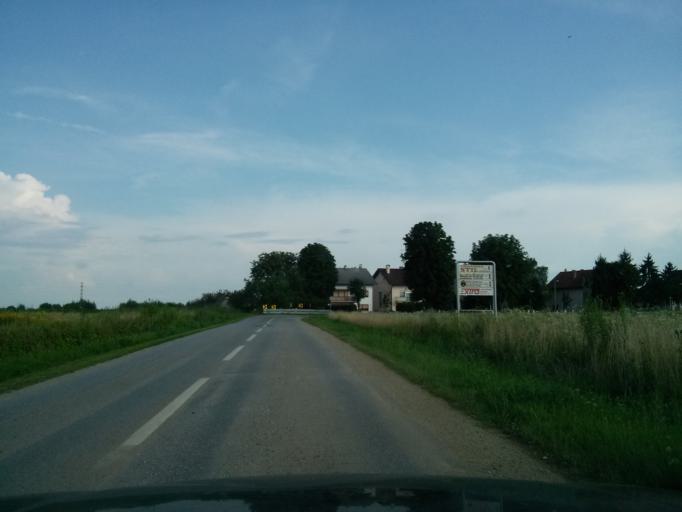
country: HR
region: Grad Zagreb
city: Zadvorsko
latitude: 45.7356
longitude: 15.9130
